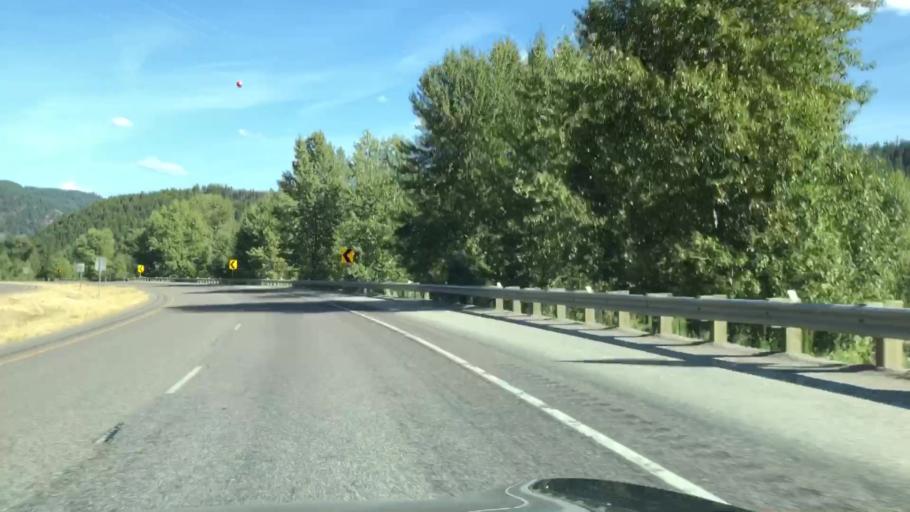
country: US
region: Montana
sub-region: Sanders County
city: Thompson Falls
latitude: 47.3755
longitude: -115.3796
